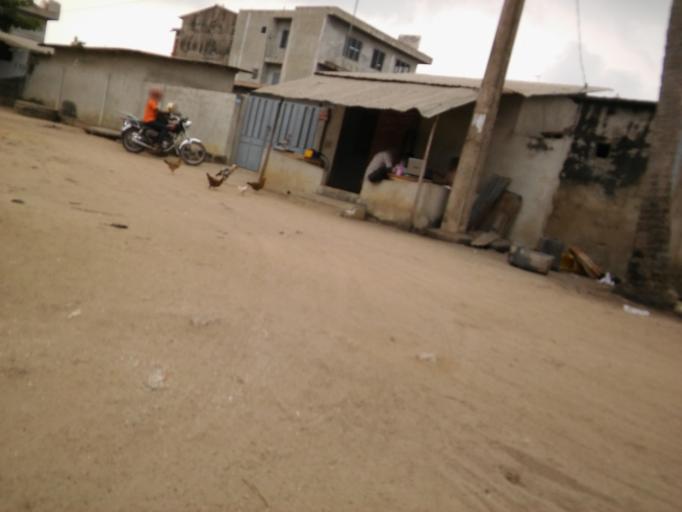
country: BJ
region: Littoral
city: Cotonou
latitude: 6.3929
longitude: 2.3702
